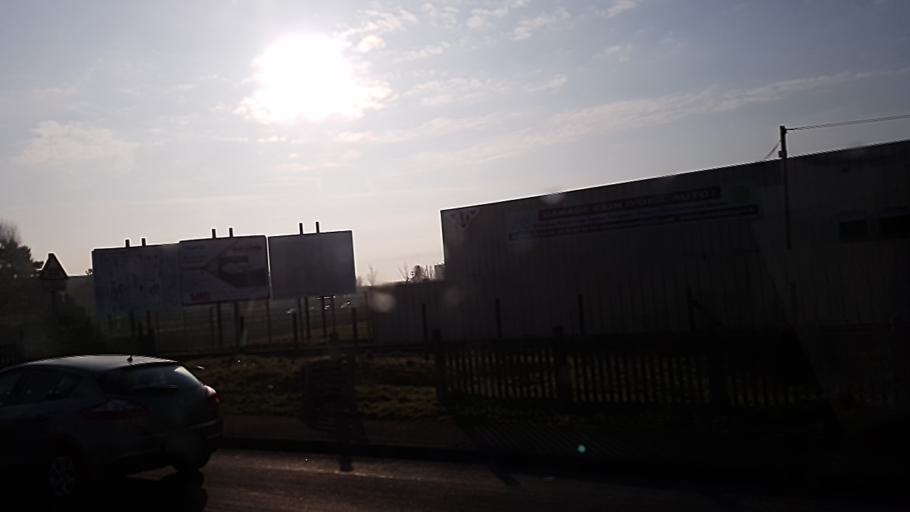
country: FR
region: Nord-Pas-de-Calais
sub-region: Departement du Nord
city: Coudekerque-Branche
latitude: 51.0236
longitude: 2.3953
